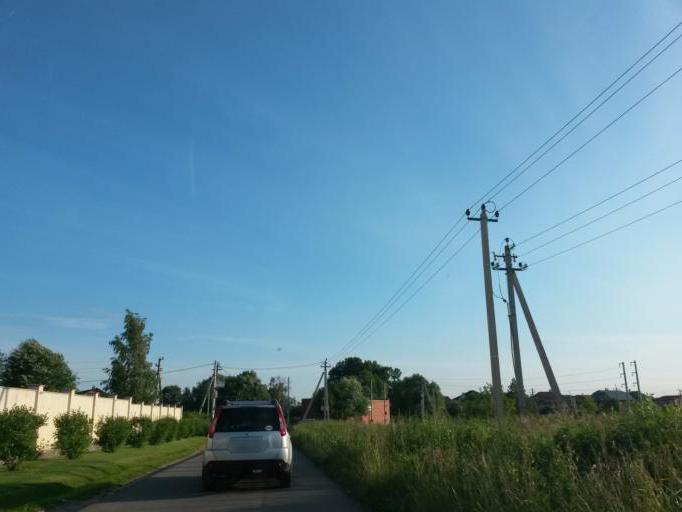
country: RU
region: Moskovskaya
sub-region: Podol'skiy Rayon
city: Podol'sk
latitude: 55.3958
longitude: 37.6206
